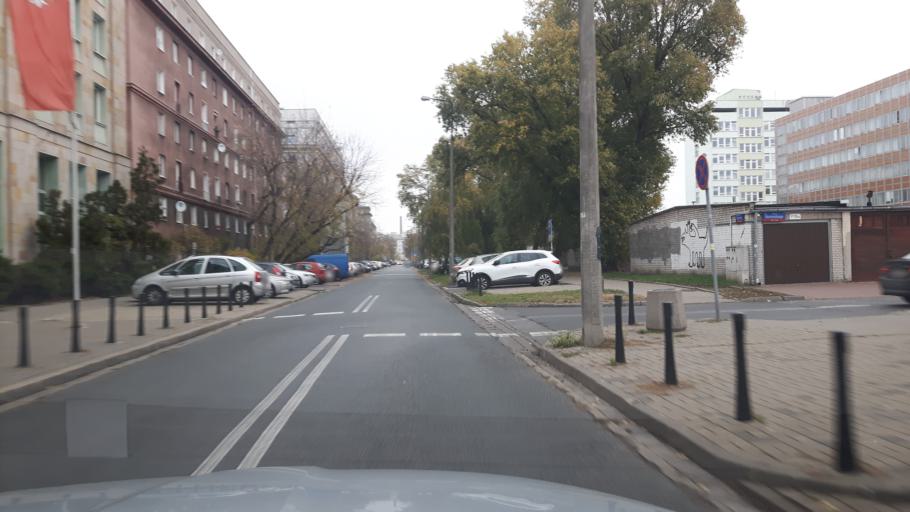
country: PL
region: Masovian Voivodeship
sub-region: Warszawa
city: Praga Polnoc
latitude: 52.2586
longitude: 21.0291
